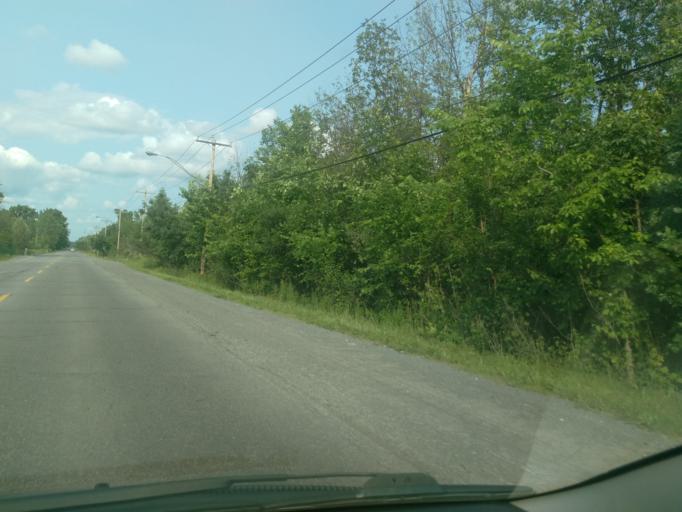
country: CA
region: Ontario
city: Ottawa
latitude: 45.4008
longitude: -75.7814
